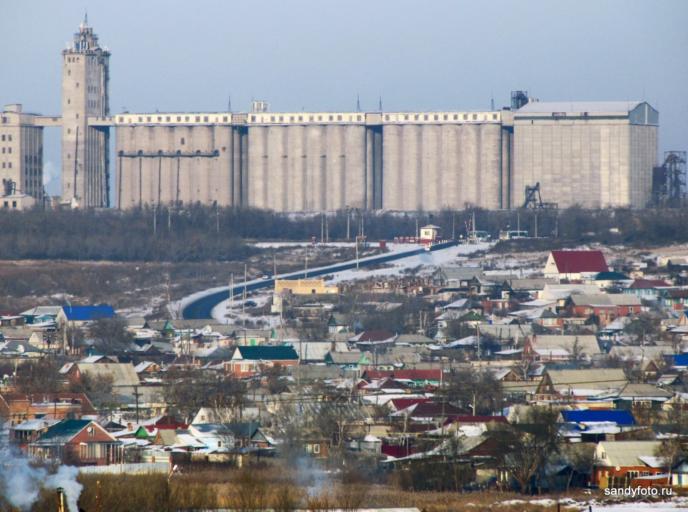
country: RU
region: Chelyabinsk
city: Troitsk
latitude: 54.0782
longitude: 61.5782
